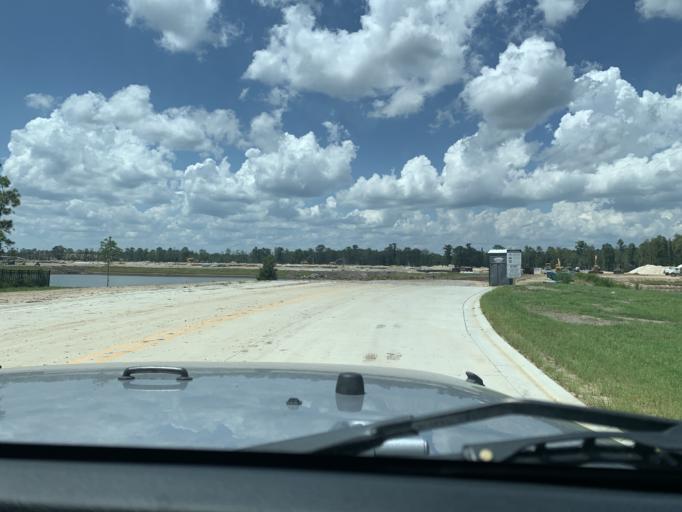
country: US
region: Georgia
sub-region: Chatham County
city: Bloomingdale
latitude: 32.1181
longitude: -81.2783
